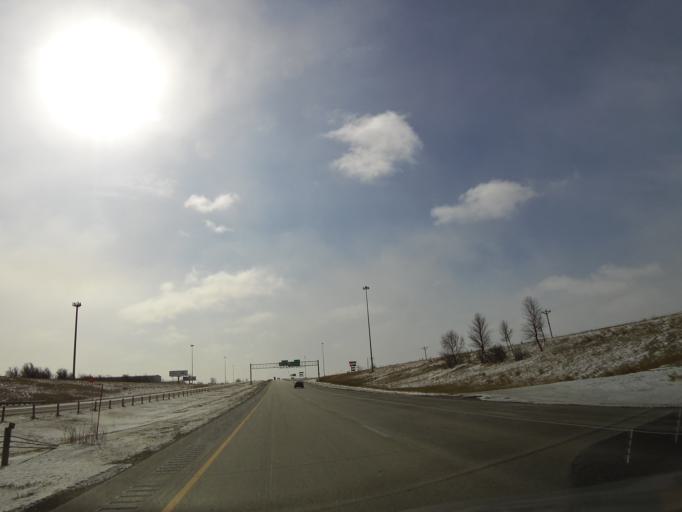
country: US
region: North Dakota
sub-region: Grand Forks County
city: Grand Forks
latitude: 47.9403
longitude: -97.0937
